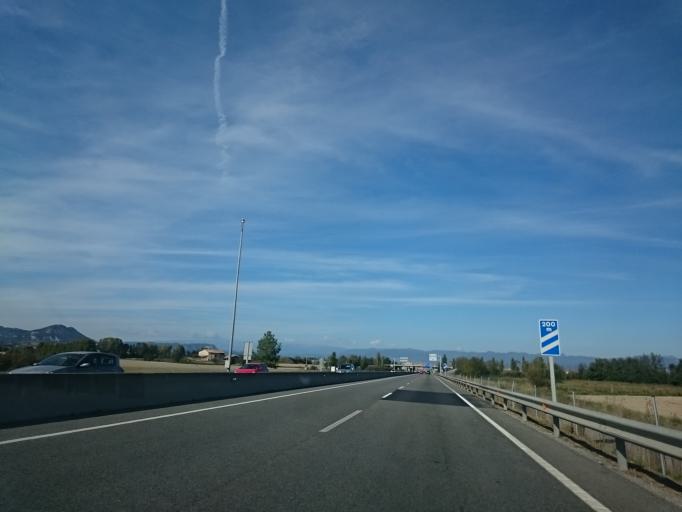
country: ES
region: Catalonia
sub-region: Provincia de Barcelona
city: Vic
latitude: 41.8993
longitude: 2.2468
